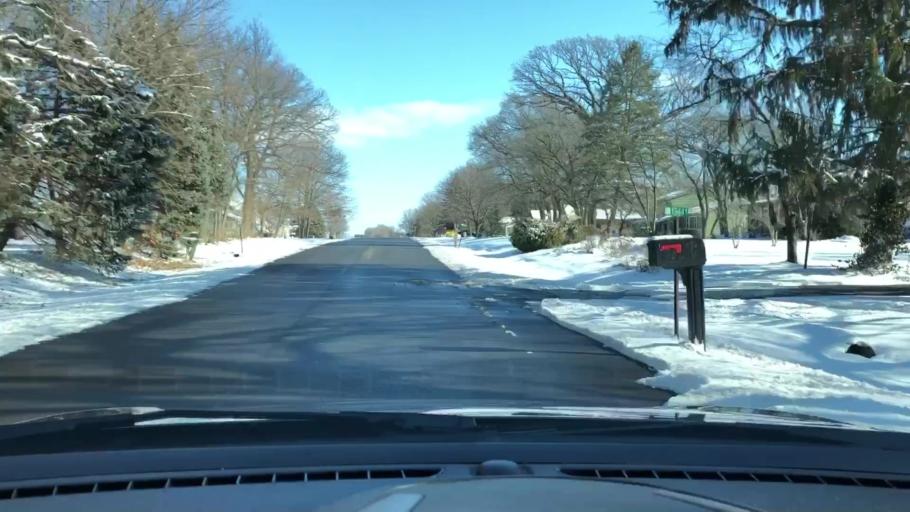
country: US
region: Illinois
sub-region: Will County
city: Elwood
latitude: 41.4370
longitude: -88.0852
